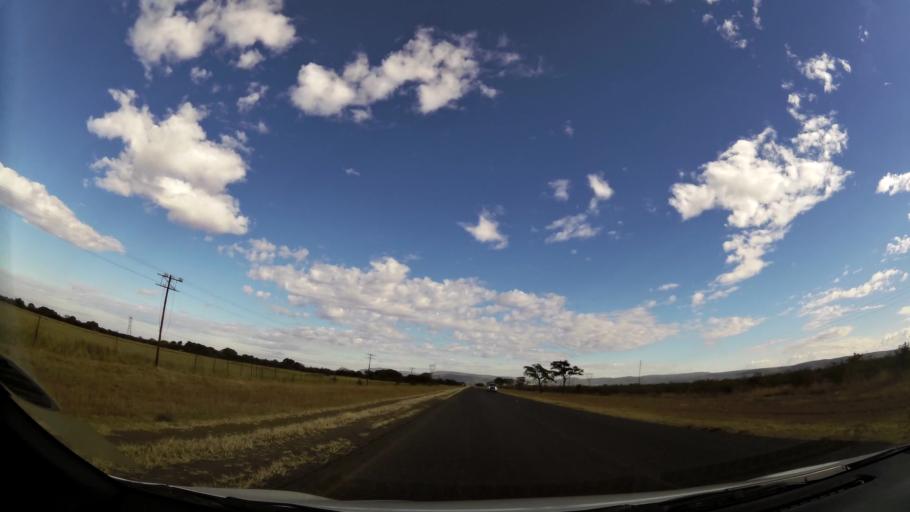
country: ZA
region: Limpopo
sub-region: Waterberg District Municipality
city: Bela-Bela
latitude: -24.9017
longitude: 28.3316
